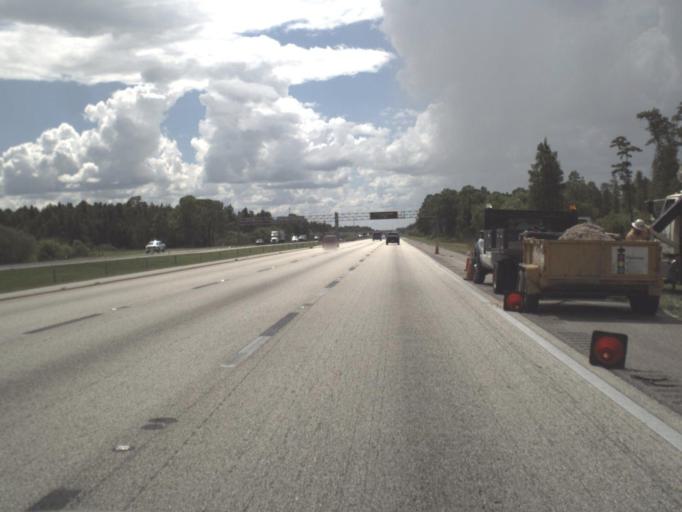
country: US
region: Florida
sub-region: Polk County
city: Polk City
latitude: 28.1873
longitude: -81.7314
